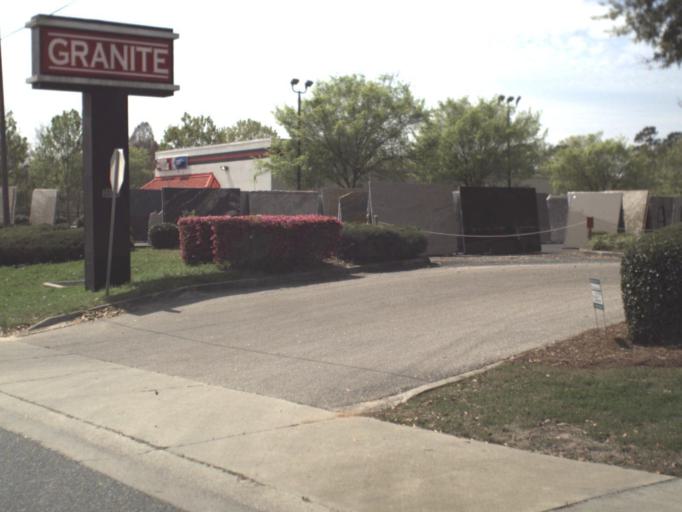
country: US
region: Florida
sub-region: Leon County
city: Tallahassee
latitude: 30.4814
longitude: -84.2369
